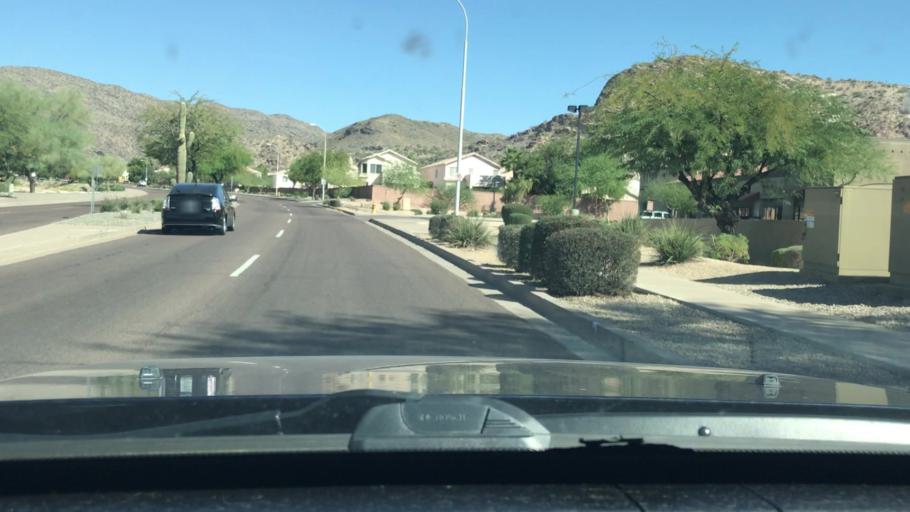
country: US
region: Arizona
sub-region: Maricopa County
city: Guadalupe
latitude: 33.3066
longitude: -112.0553
